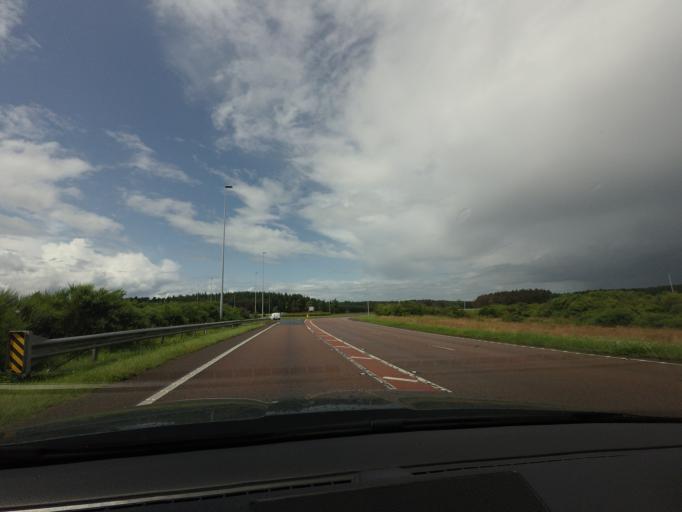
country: GB
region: Scotland
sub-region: Moray
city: Fochabers
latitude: 57.6257
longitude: -3.1411
